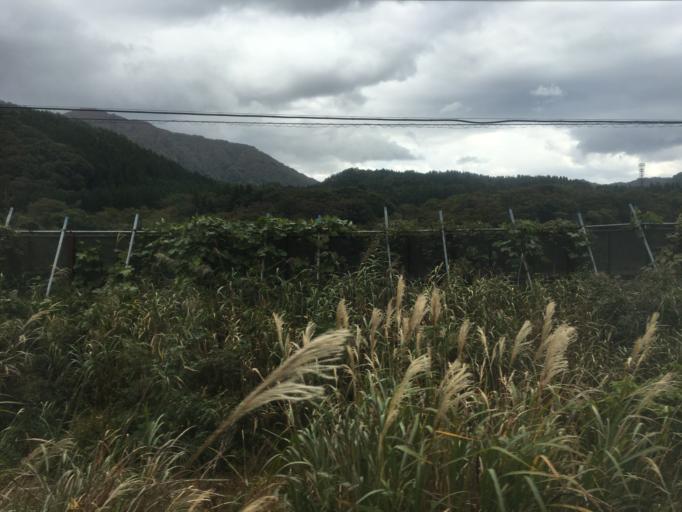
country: JP
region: Niigata
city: Murakami
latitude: 38.0681
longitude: 139.6634
